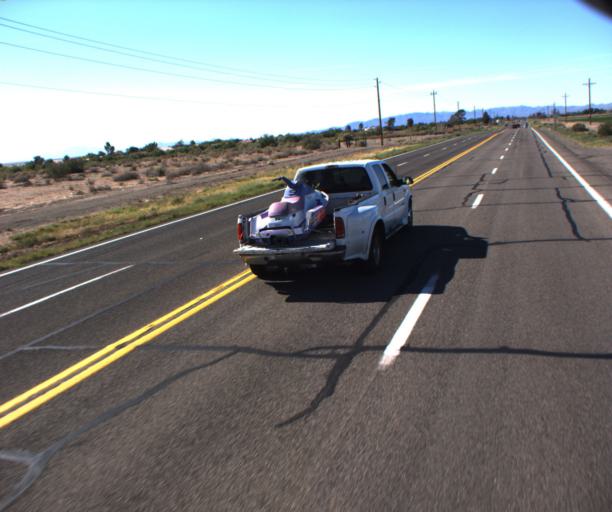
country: US
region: Arizona
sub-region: Mohave County
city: Mohave Valley
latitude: 34.9368
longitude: -114.5980
